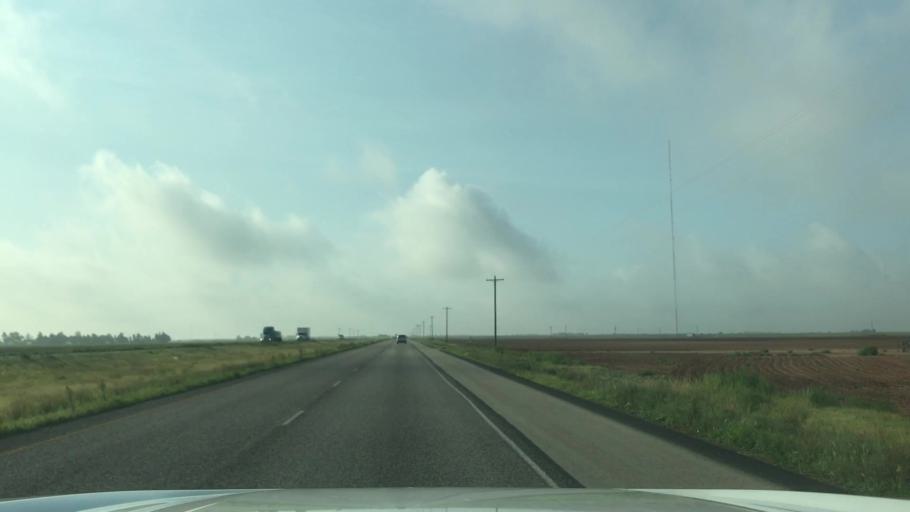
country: US
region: Texas
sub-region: Garza County
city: Post
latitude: 33.2314
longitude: -101.4468
